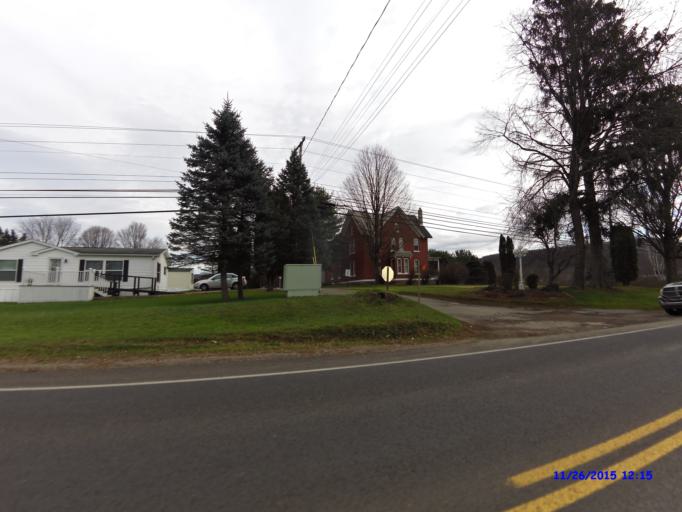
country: US
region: New York
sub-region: Cattaraugus County
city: Allegany
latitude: 42.1252
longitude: -78.5011
